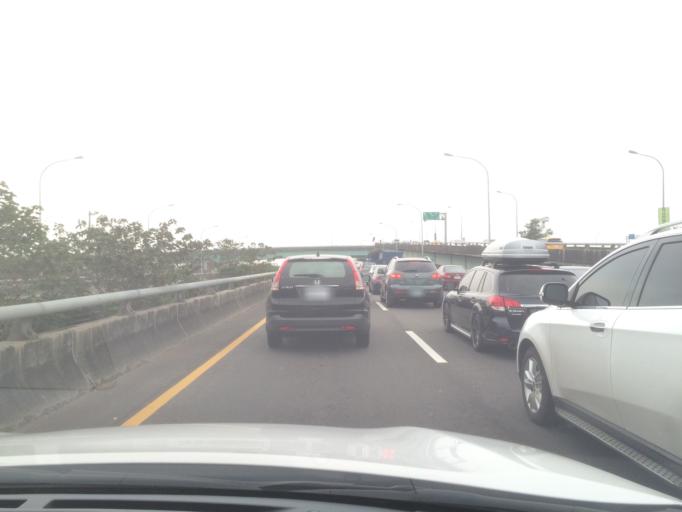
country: TW
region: Taiwan
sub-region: Taichung City
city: Taichung
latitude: 24.1224
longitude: 120.6197
